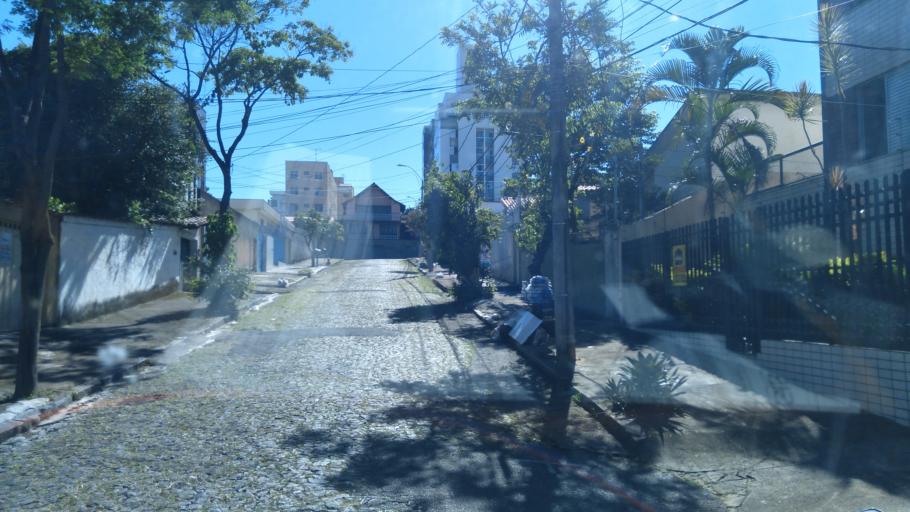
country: BR
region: Minas Gerais
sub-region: Belo Horizonte
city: Belo Horizonte
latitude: -19.8812
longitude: -43.9114
